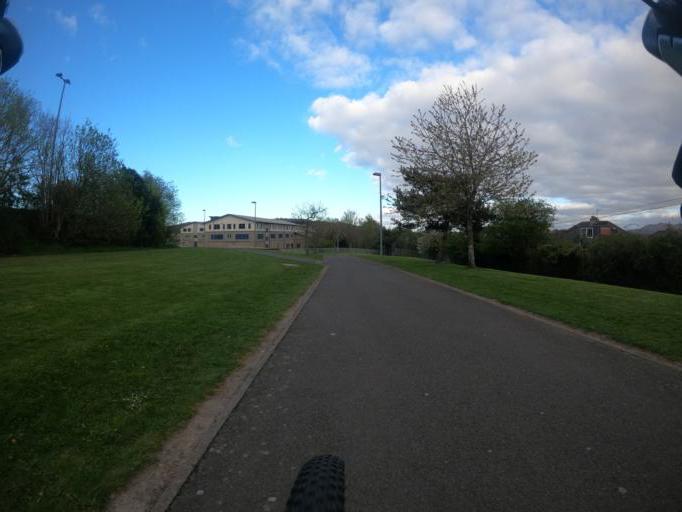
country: GB
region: Scotland
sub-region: Edinburgh
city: Currie
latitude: 55.9445
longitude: -3.3072
